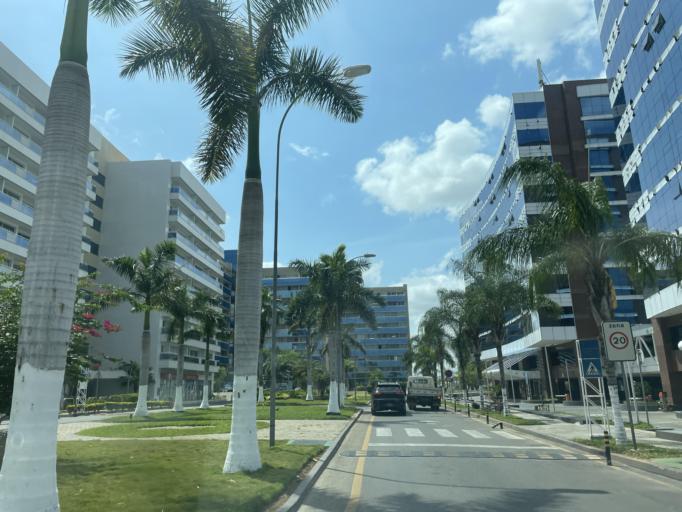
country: AO
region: Luanda
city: Luanda
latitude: -8.9216
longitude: 13.1885
